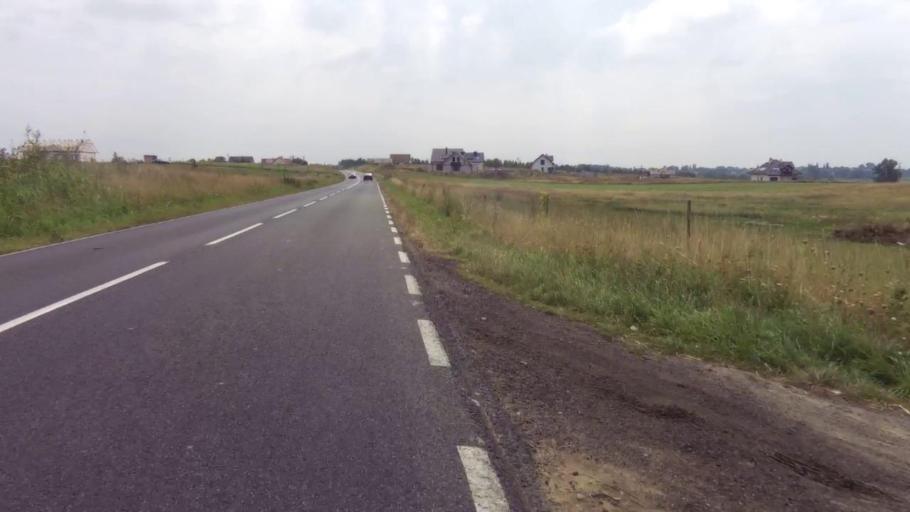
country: PL
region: West Pomeranian Voivodeship
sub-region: Powiat choszczenski
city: Choszczno
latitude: 53.1819
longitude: 15.4033
